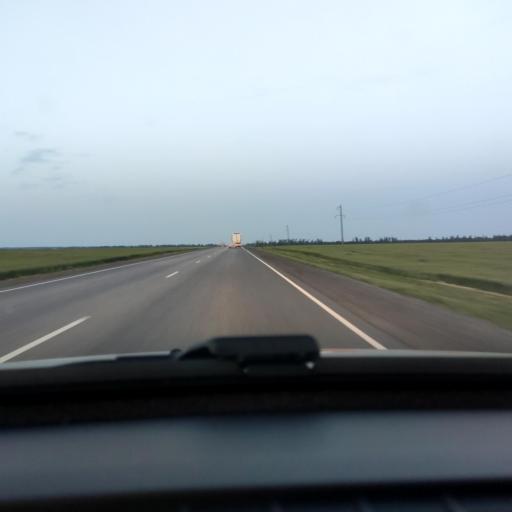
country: RU
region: Voronezj
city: Volya
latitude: 51.6879
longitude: 39.5147
